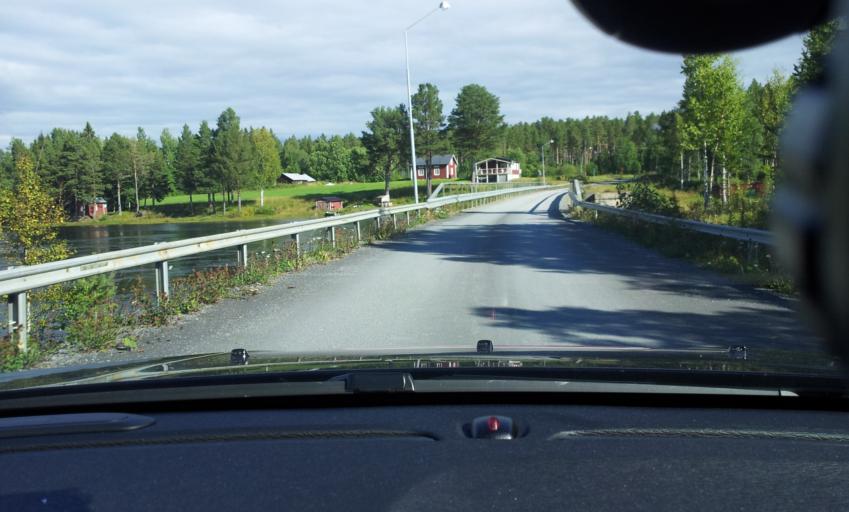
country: SE
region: Jaemtland
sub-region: Are Kommun
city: Jarpen
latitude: 63.2824
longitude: 13.7295
